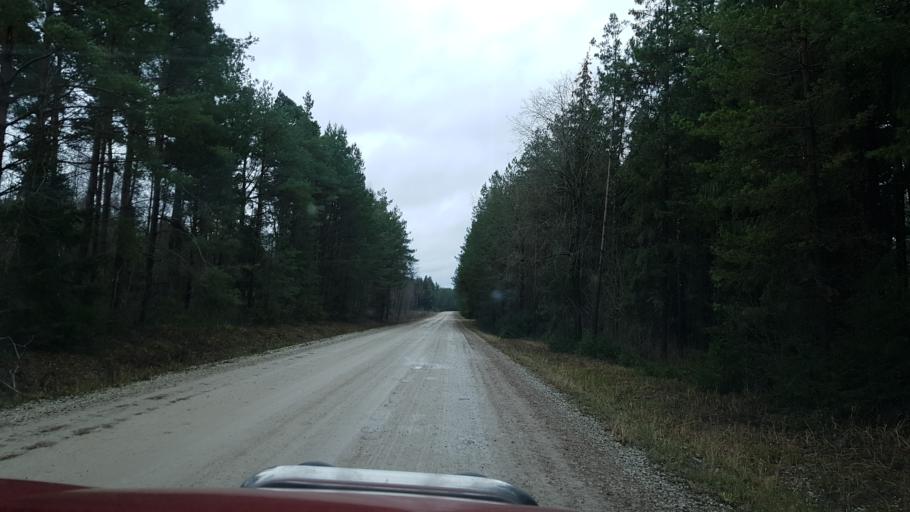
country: EE
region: Paernumaa
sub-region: Halinga vald
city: Parnu-Jaagupi
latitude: 58.5503
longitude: 24.4118
